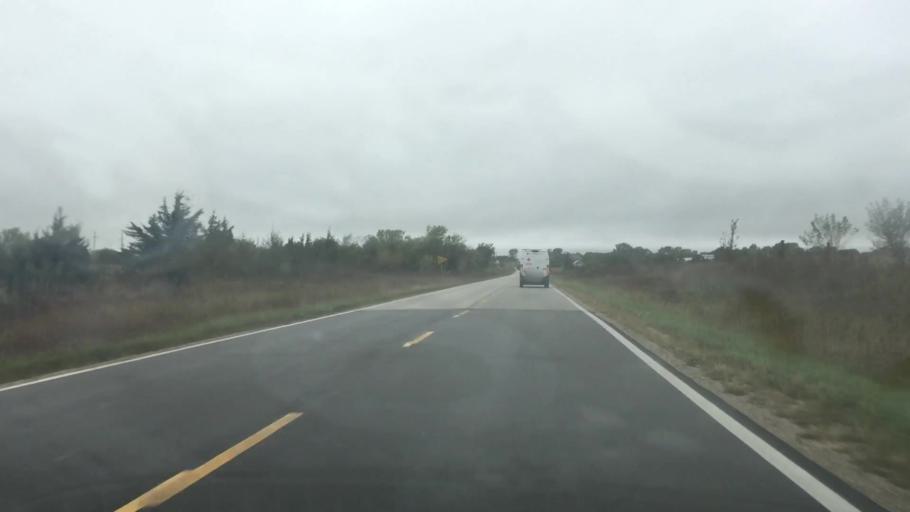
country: US
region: Kansas
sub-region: Anderson County
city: Garnett
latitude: 38.1717
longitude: -95.2826
